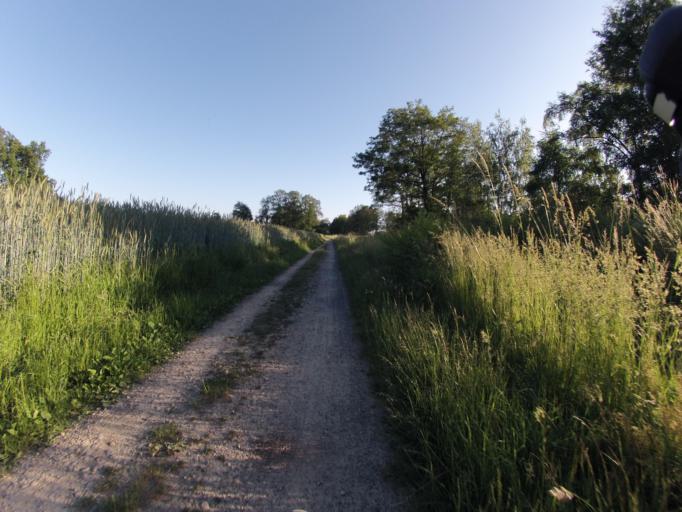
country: NL
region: Overijssel
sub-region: Gemeente Losser
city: Losser
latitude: 52.2923
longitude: 7.0799
